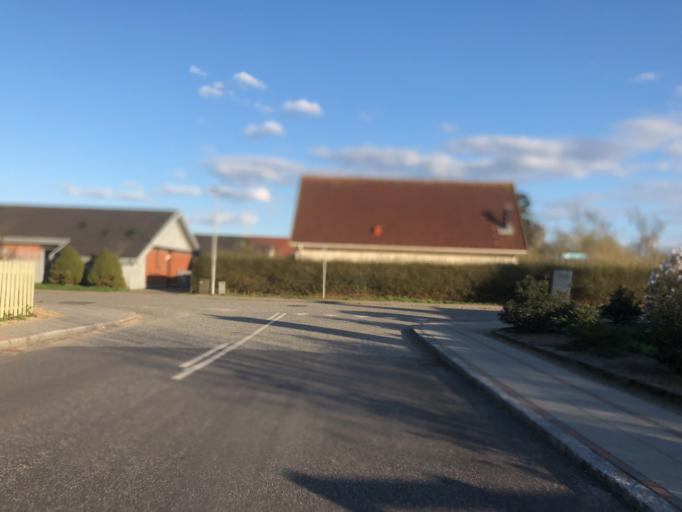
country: DK
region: Zealand
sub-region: Ringsted Kommune
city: Ringsted
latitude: 55.4612
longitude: 11.7972
